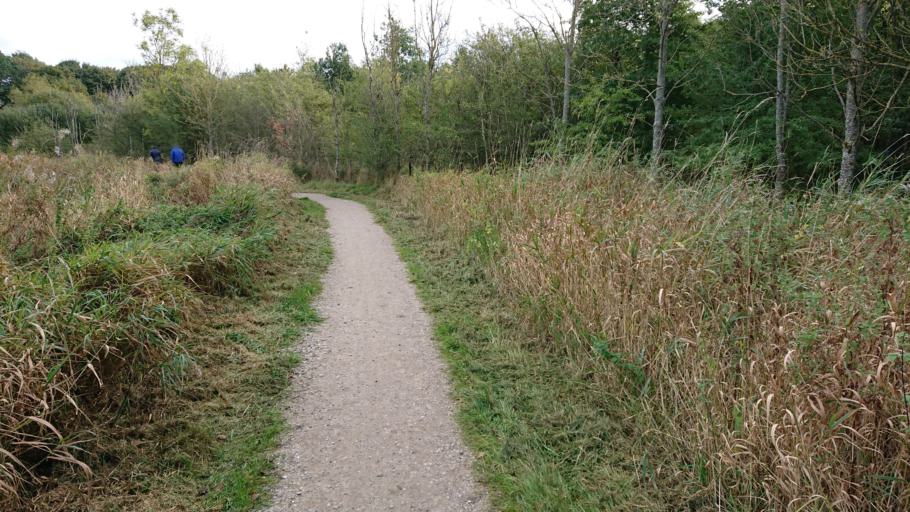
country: DK
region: Central Jutland
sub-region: Arhus Kommune
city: Stavtrup
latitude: 56.1712
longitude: 10.1072
